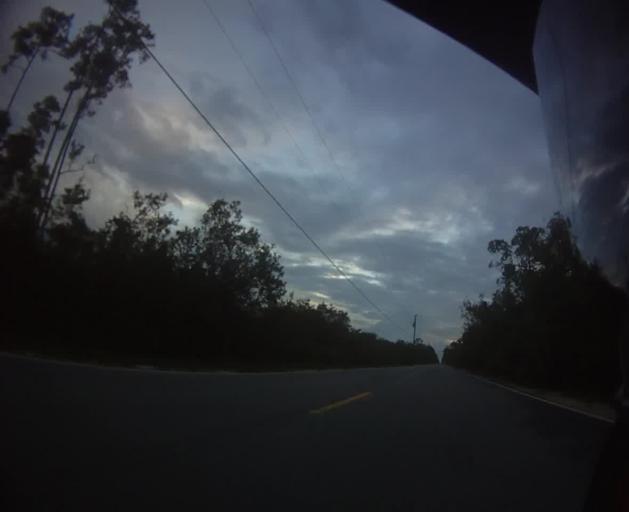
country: US
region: Florida
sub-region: Miami-Dade County
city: Florida City
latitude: 25.3894
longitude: -80.6477
